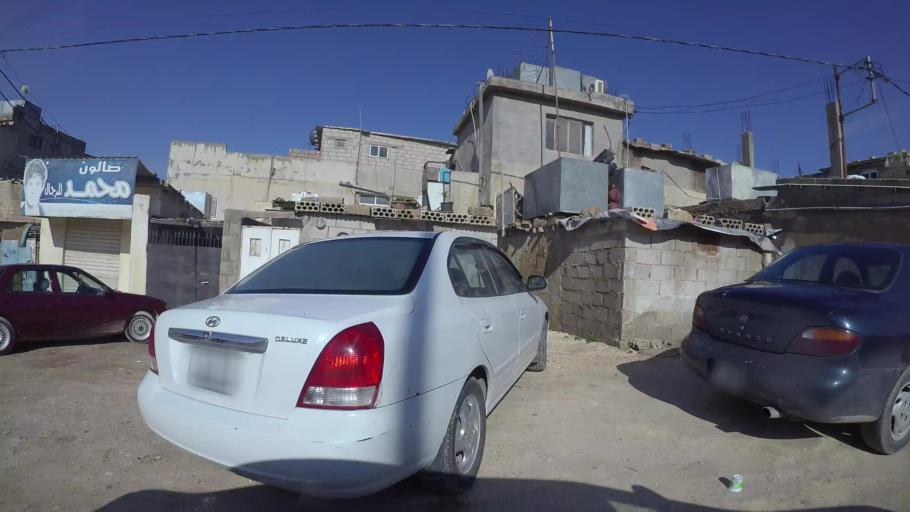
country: JO
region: Amman
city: Al Jubayhah
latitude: 32.0703
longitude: 35.8468
